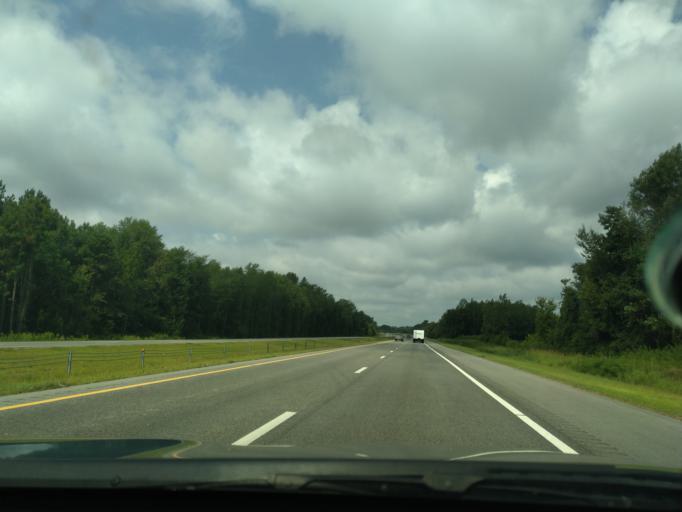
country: US
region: North Carolina
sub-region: Martin County
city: Robersonville
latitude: 35.8331
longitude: -77.3038
